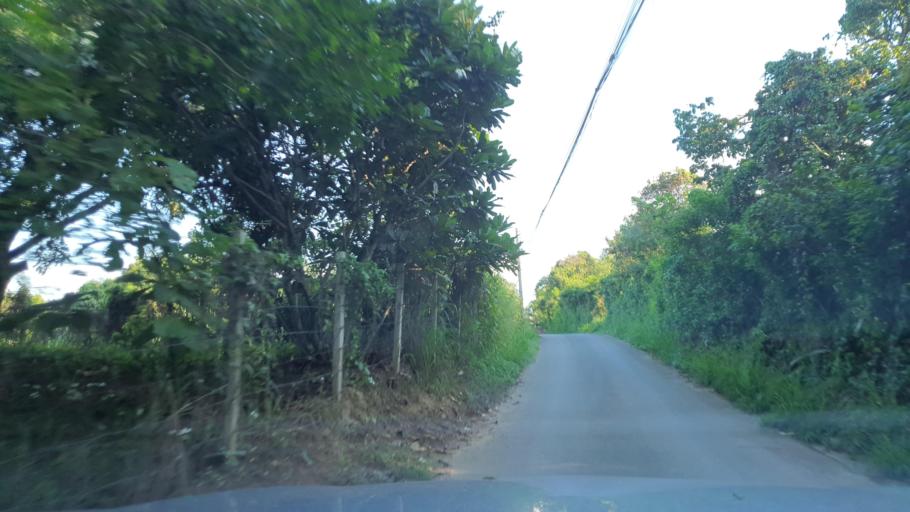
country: TH
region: Chiang Mai
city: Hang Dong
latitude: 18.6850
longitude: 98.8882
